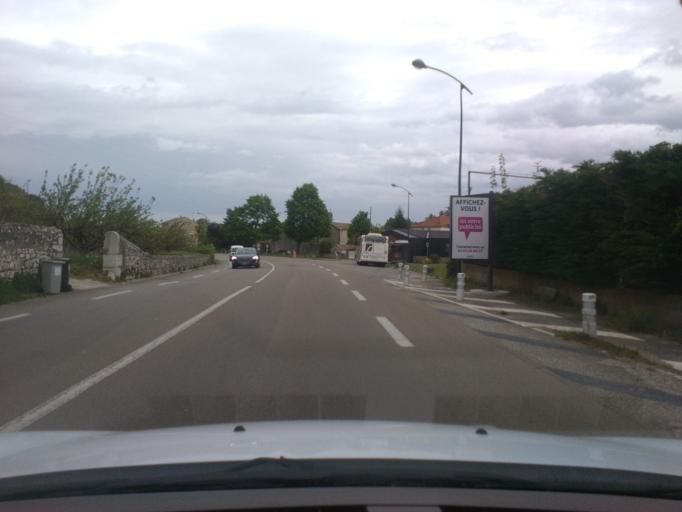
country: FR
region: Rhone-Alpes
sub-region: Departement de l'Ardeche
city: Cornas
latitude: 44.9715
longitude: 4.8516
